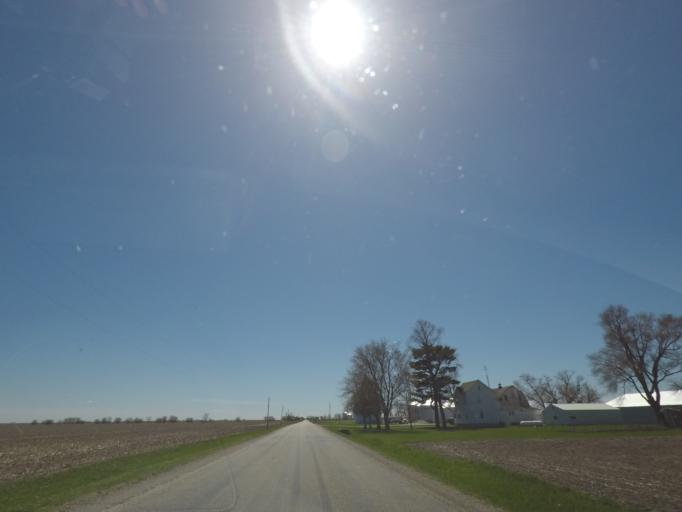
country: US
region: Illinois
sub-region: Logan County
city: Atlanta
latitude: 40.2005
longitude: -89.1942
